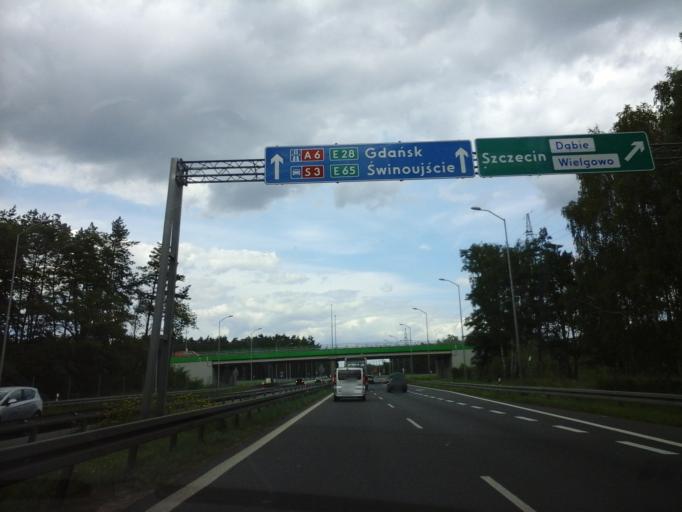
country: PL
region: West Pomeranian Voivodeship
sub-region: Powiat gryfinski
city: Stare Czarnowo
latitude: 53.3937
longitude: 14.7178
